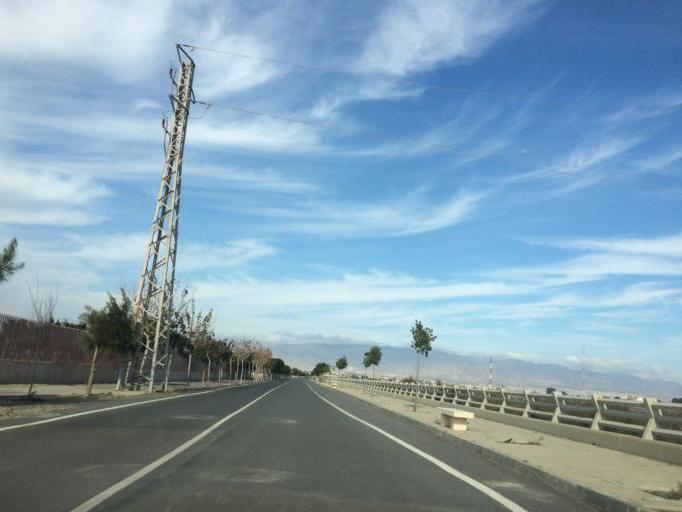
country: ES
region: Andalusia
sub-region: Provincia de Almeria
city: Almeria
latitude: 36.8163
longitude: -2.4299
